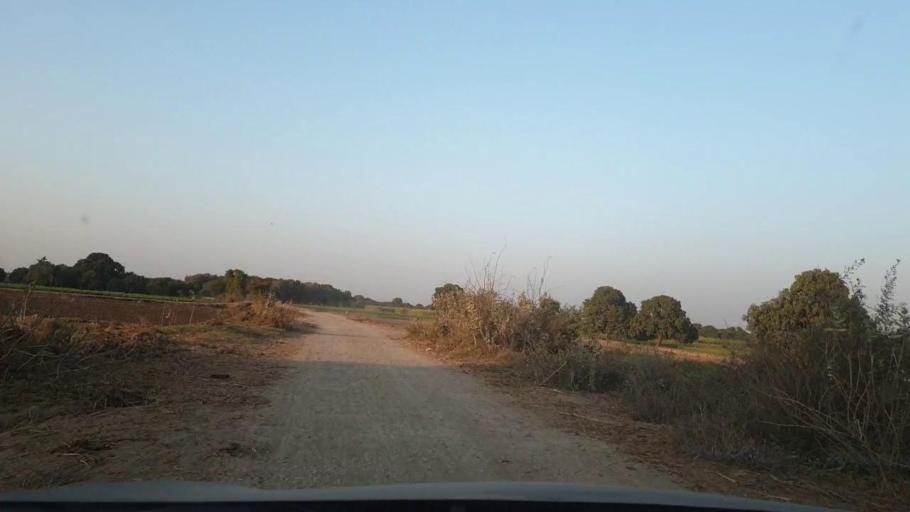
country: PK
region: Sindh
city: Tando Allahyar
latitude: 25.5070
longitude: 68.7410
